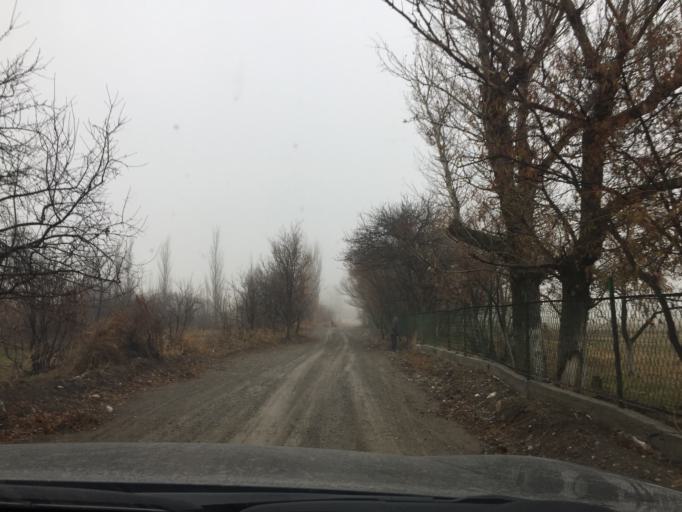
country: KZ
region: Ongtustik Qazaqstan
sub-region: Tulkibas Audany
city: Zhabagly
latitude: 42.5131
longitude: 70.5622
